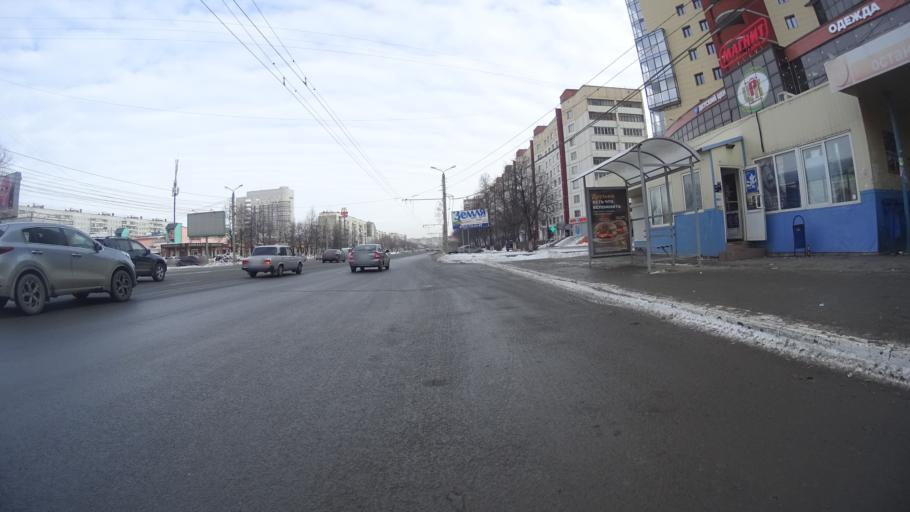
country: RU
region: Chelyabinsk
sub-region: Gorod Chelyabinsk
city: Chelyabinsk
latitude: 55.1944
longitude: 61.3420
